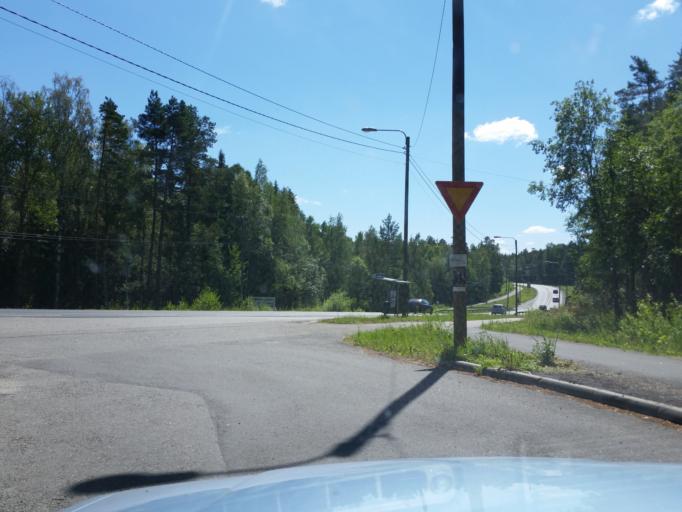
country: FI
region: Varsinais-Suomi
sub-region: Turku
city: Kaarina
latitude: 60.3490
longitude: 22.3599
